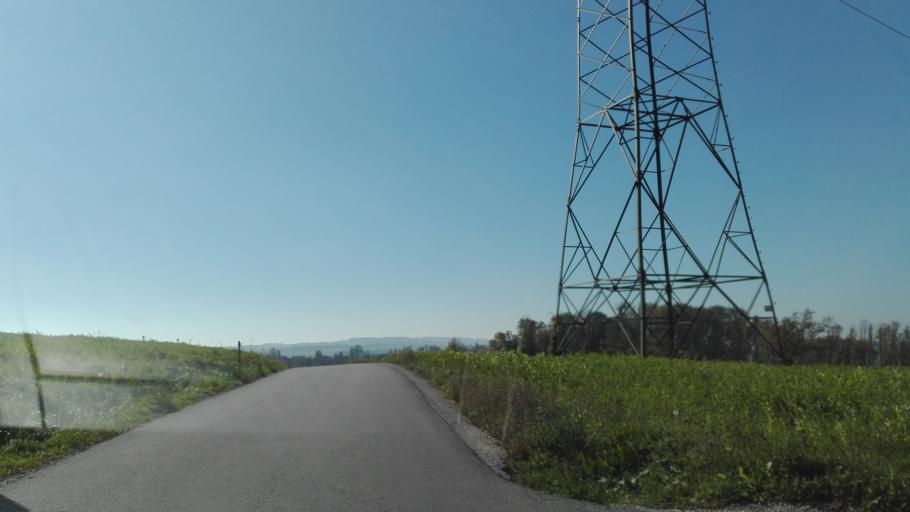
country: AT
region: Upper Austria
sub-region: Politischer Bezirk Linz-Land
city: Pasching
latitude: 48.2863
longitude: 14.1714
